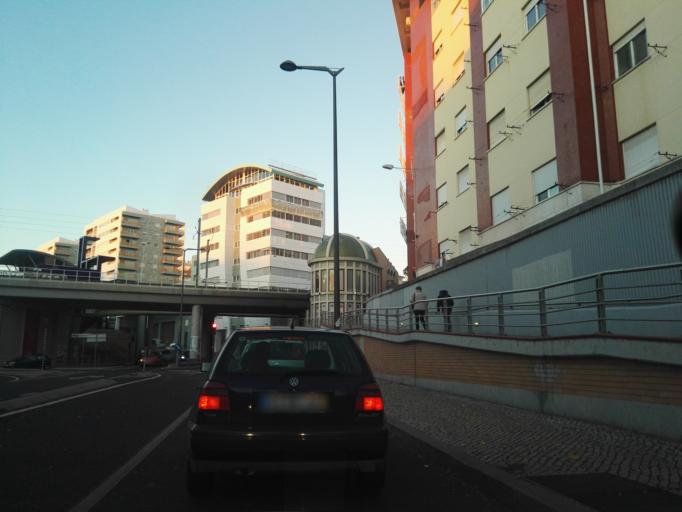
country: PT
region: Lisbon
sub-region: Oeiras
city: Paco de Arcos
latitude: 38.6965
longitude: -9.2926
